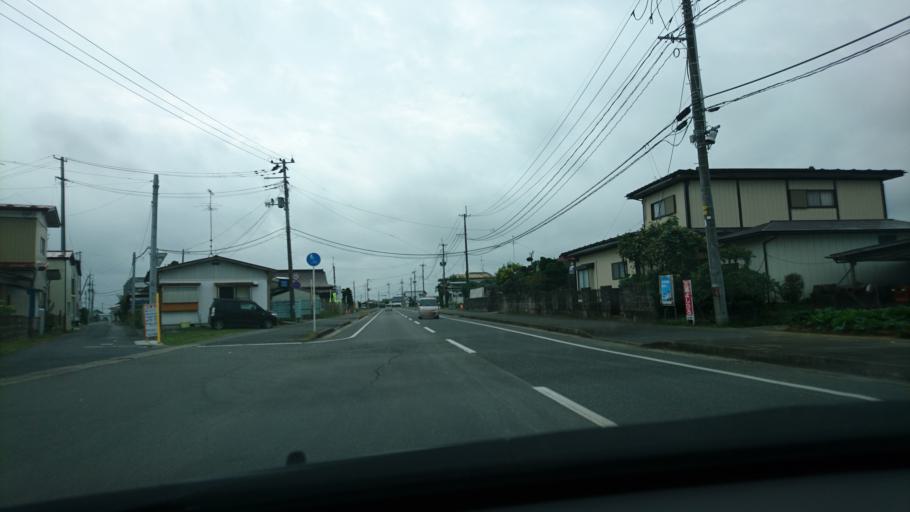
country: JP
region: Iwate
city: Ichinoseki
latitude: 38.7700
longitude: 141.1398
